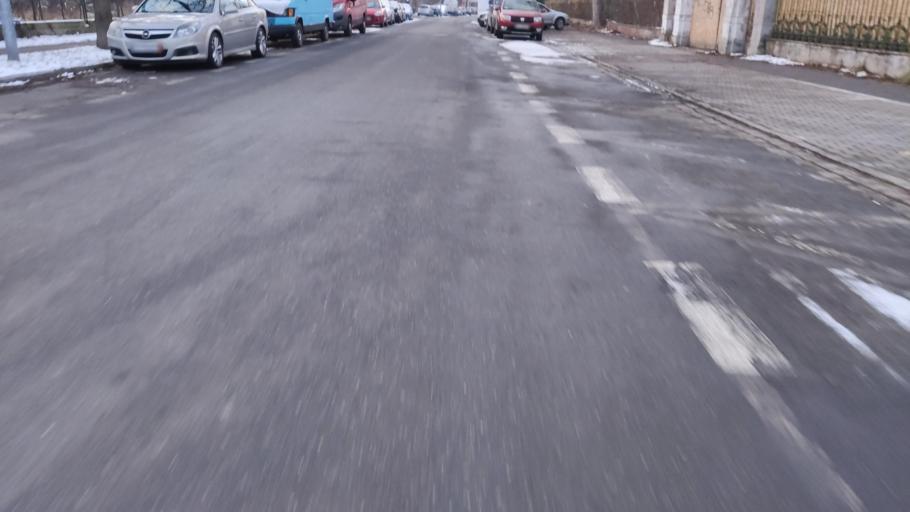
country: PL
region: Lower Silesian Voivodeship
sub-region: Powiat wroclawski
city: Wroclaw
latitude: 51.0831
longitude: 17.0138
